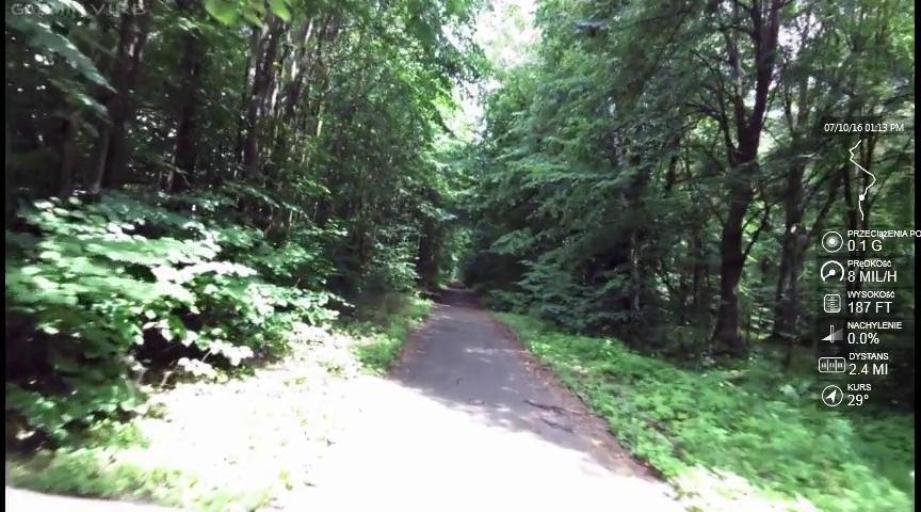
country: PL
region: West Pomeranian Voivodeship
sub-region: Powiat gryfinski
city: Banie
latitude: 53.0707
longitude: 14.6304
